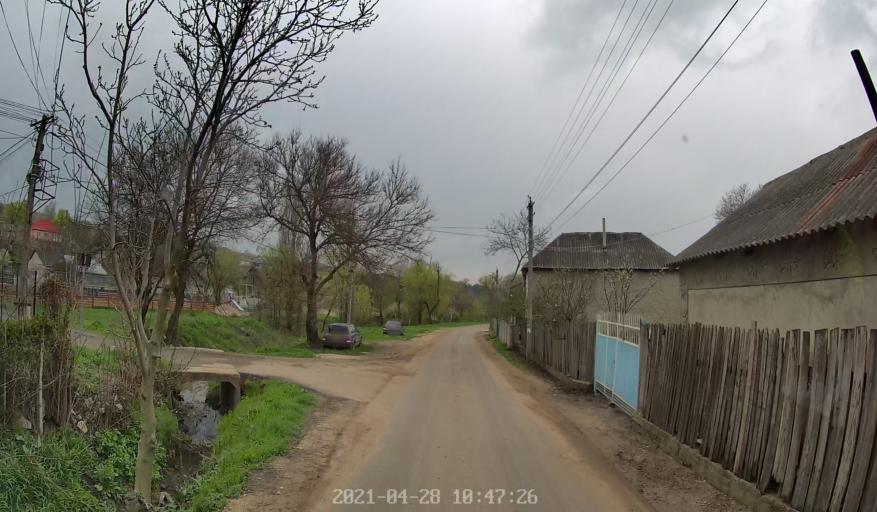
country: MD
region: Chisinau
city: Singera
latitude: 46.9890
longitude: 28.9479
